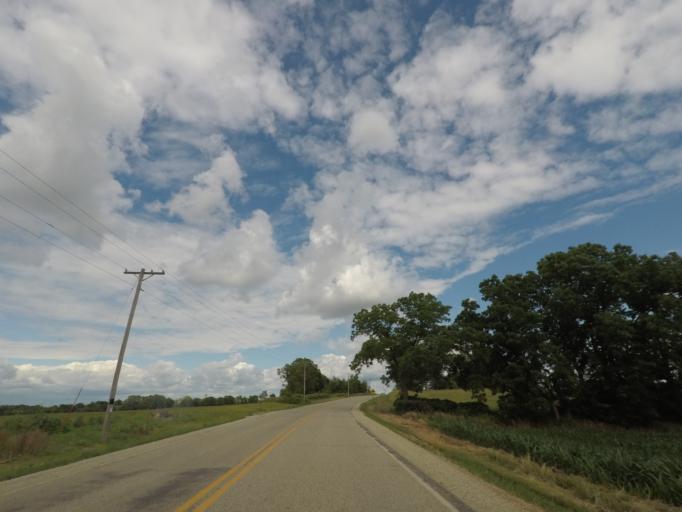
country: US
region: Wisconsin
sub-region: Rock County
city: Evansville
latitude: 42.7157
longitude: -89.2405
